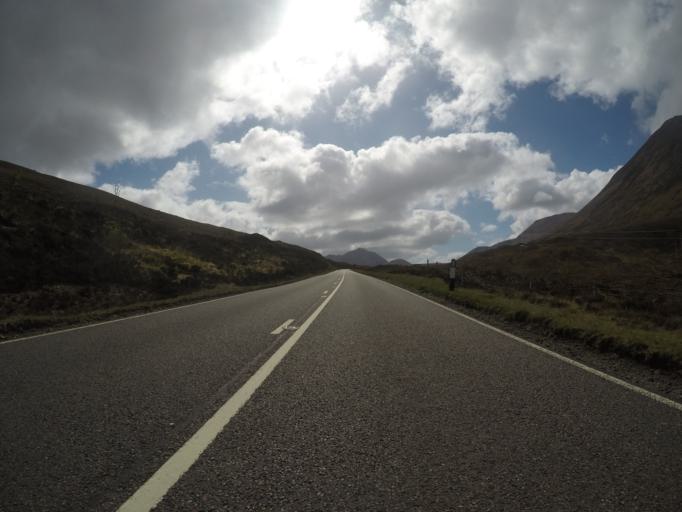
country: GB
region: Scotland
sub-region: Highland
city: Portree
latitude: 57.2867
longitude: -6.0940
